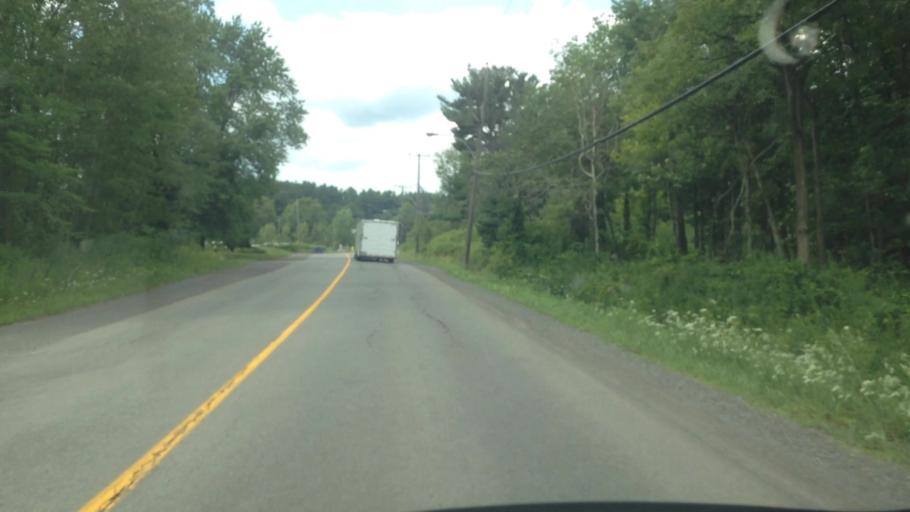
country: CA
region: Quebec
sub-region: Laurentides
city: Saint-Jerome
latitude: 45.7752
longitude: -74.0230
